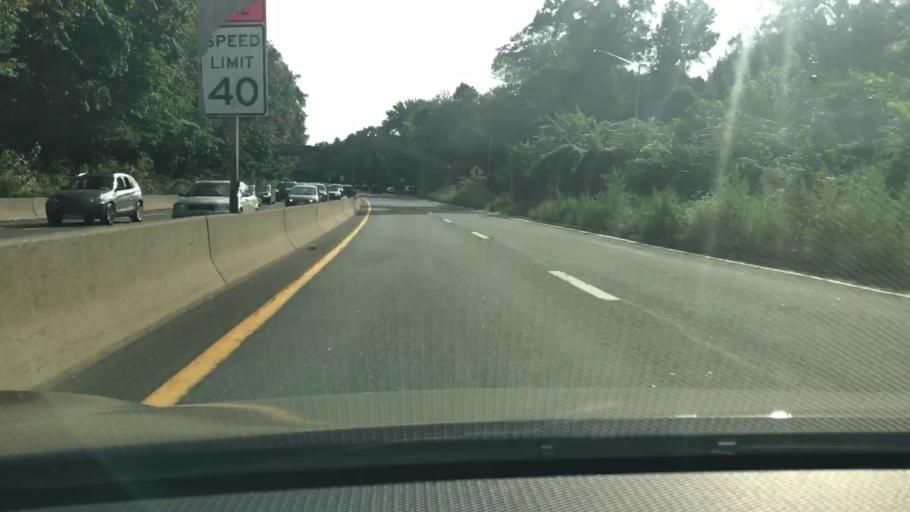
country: US
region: New York
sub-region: Westchester County
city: Pelham
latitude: 40.9211
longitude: -73.8100
